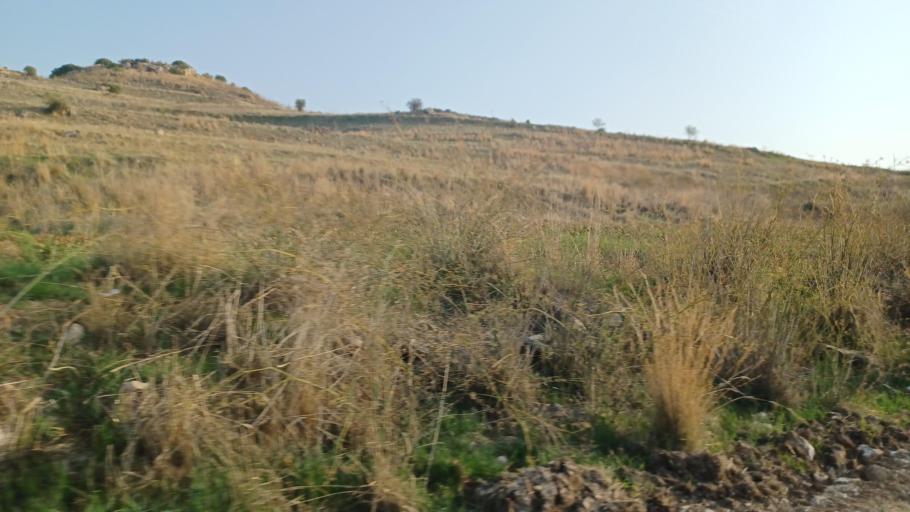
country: CY
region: Pafos
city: Polis
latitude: 34.9600
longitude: 32.4897
